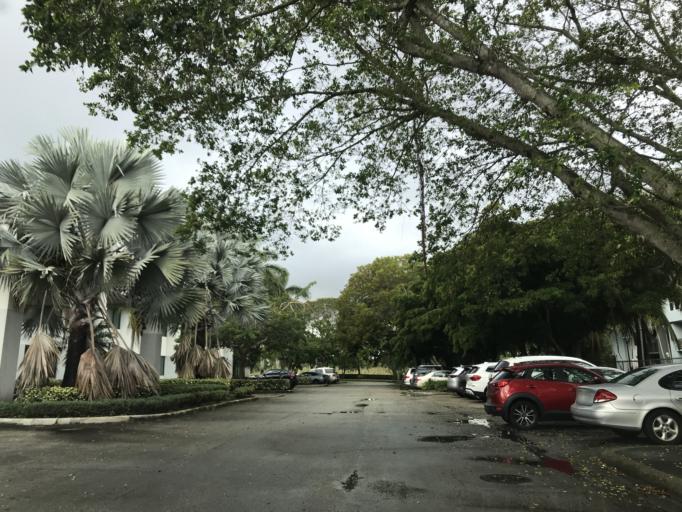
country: US
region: Florida
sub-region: Palm Beach County
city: Delray Beach
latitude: 26.4541
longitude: -80.0951
